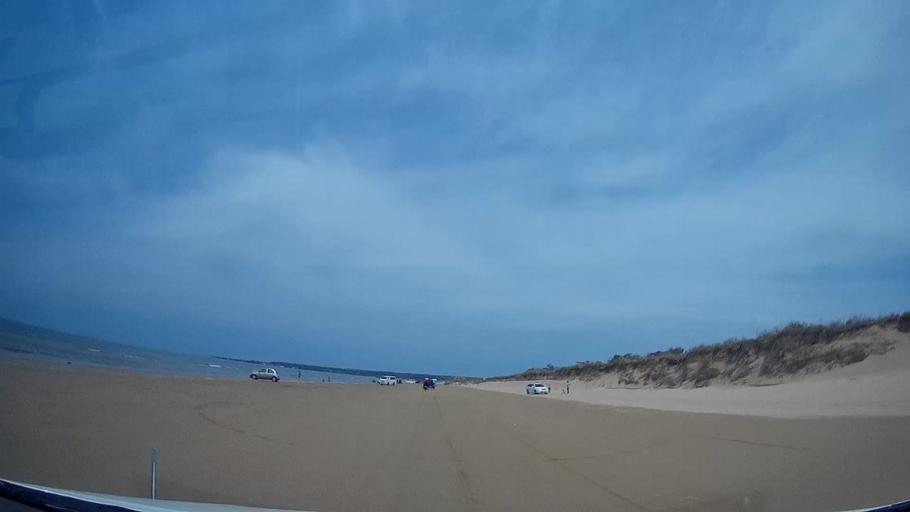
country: JP
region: Ishikawa
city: Hakui
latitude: 36.8834
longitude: 136.7632
